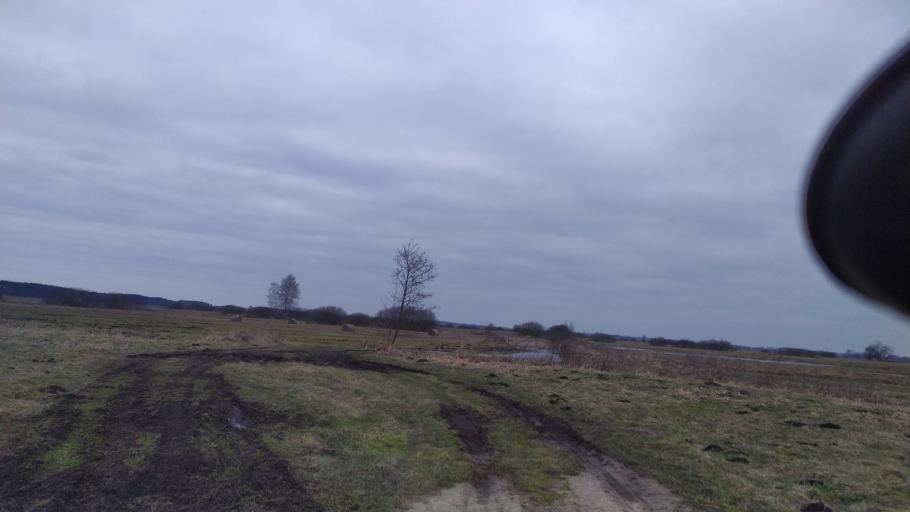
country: PL
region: Lublin Voivodeship
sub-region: Powiat lubartowski
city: Abramow
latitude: 51.4296
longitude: 22.3267
